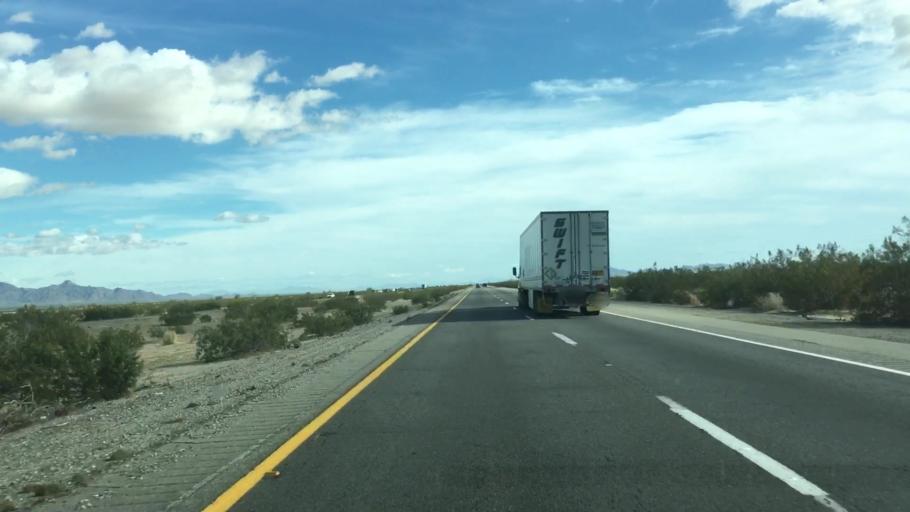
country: US
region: California
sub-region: Riverside County
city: Mesa Verde
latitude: 33.6276
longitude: -115.0628
